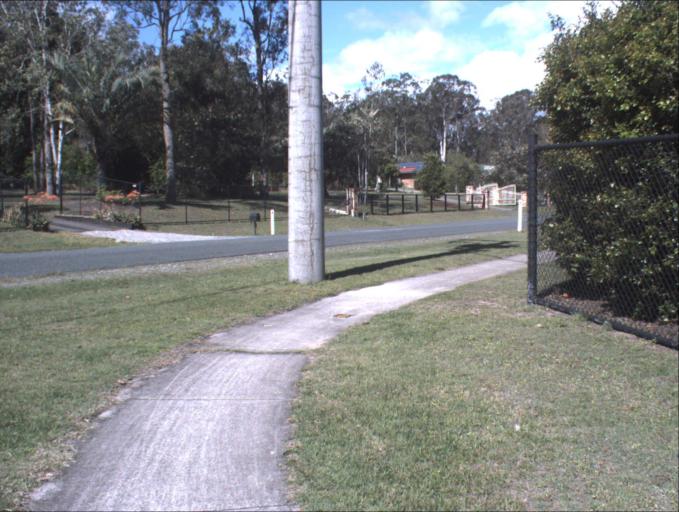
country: AU
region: Queensland
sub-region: Logan
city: Park Ridge South
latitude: -27.7397
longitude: 153.0311
